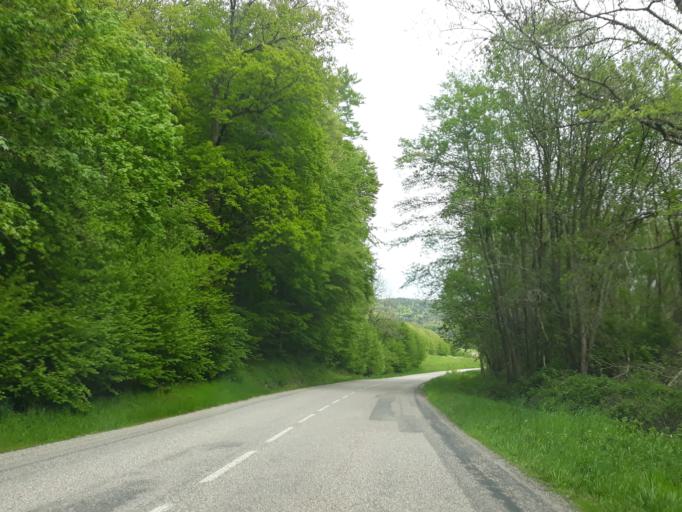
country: FR
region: Lorraine
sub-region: Departement des Vosges
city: Granges-sur-Vologne
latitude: 48.1762
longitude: 6.7648
